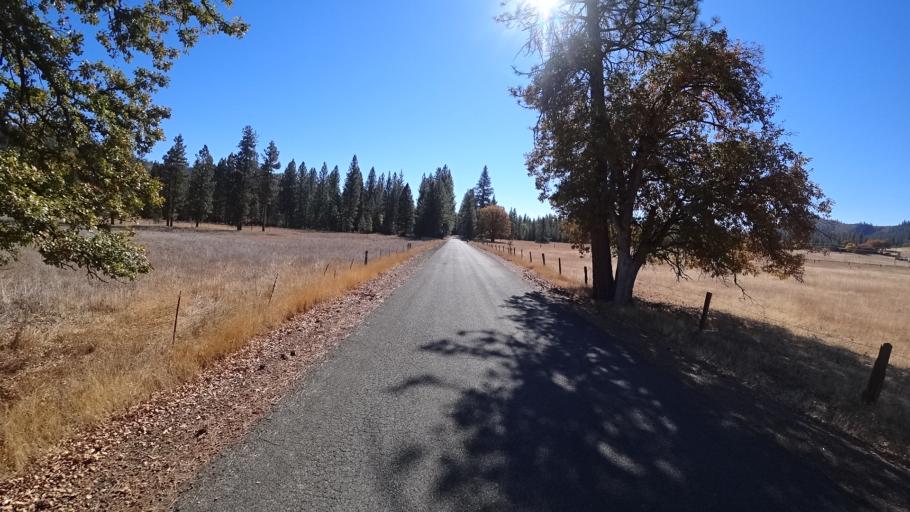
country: US
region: California
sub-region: Siskiyou County
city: Yreka
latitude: 41.5896
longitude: -122.9115
